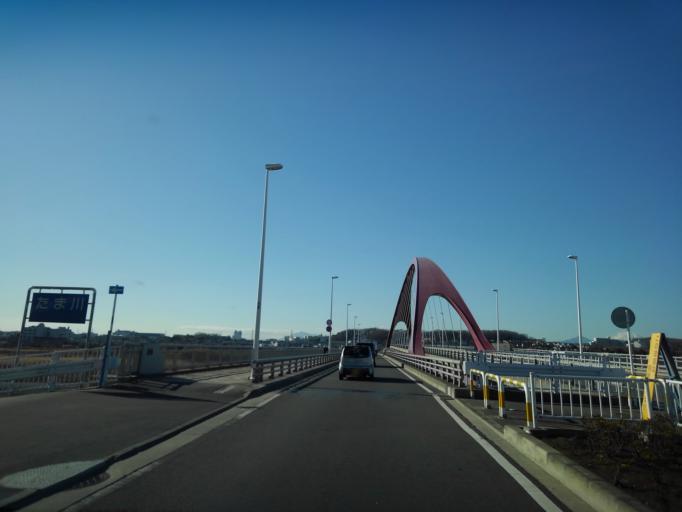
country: JP
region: Tokyo
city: Hino
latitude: 35.6951
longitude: 139.3748
